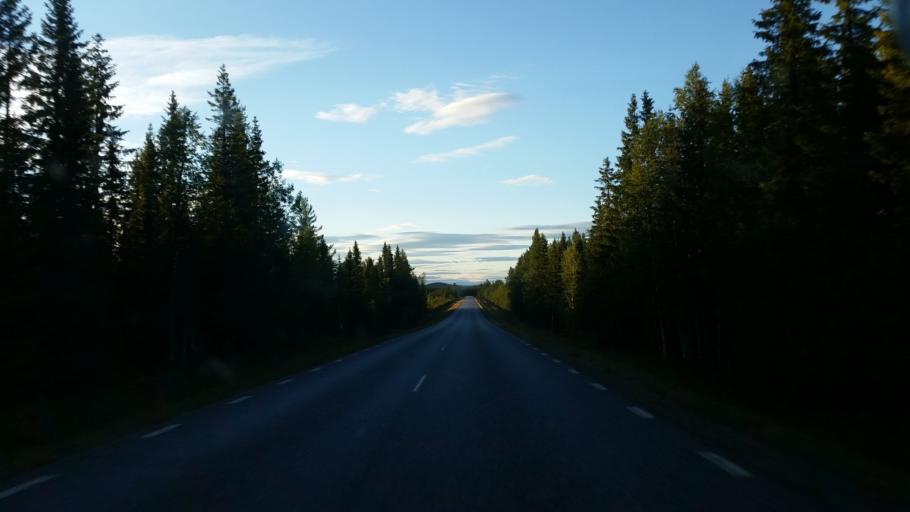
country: SE
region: Vaesterbotten
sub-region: Storumans Kommun
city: Storuman
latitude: 64.8670
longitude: 16.9917
